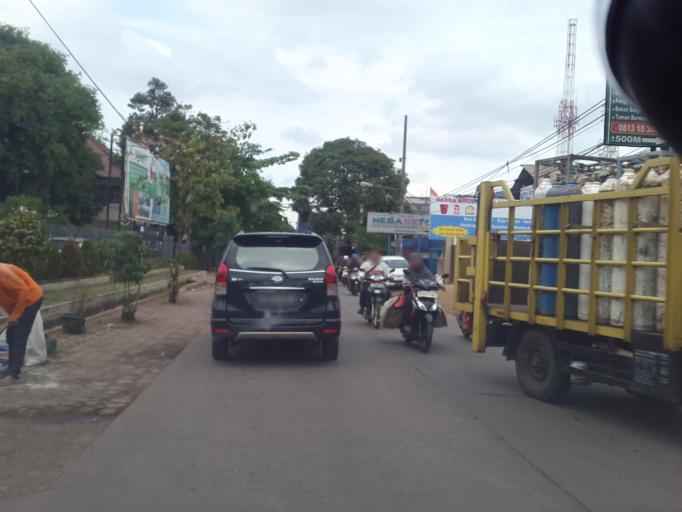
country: ID
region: West Java
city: Cileungsir
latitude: -6.3468
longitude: 106.9226
